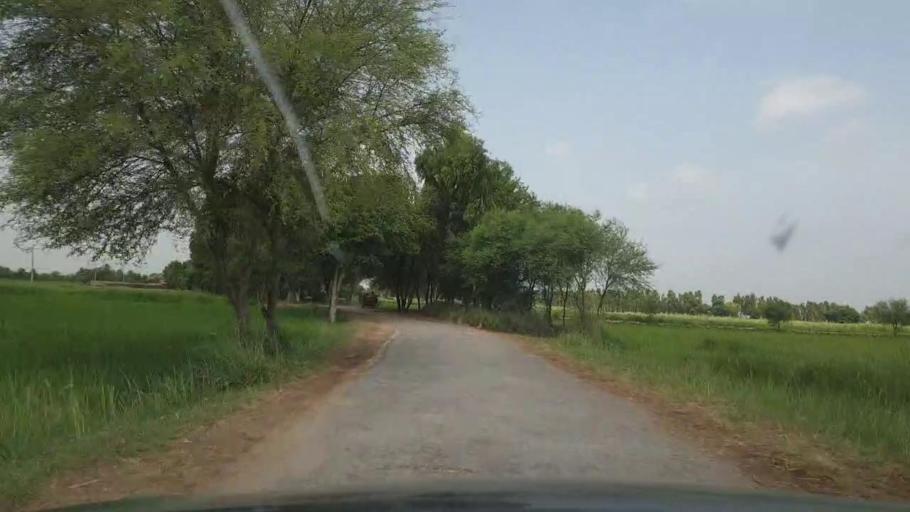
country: PK
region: Sindh
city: Ratodero
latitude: 27.8578
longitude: 68.2955
